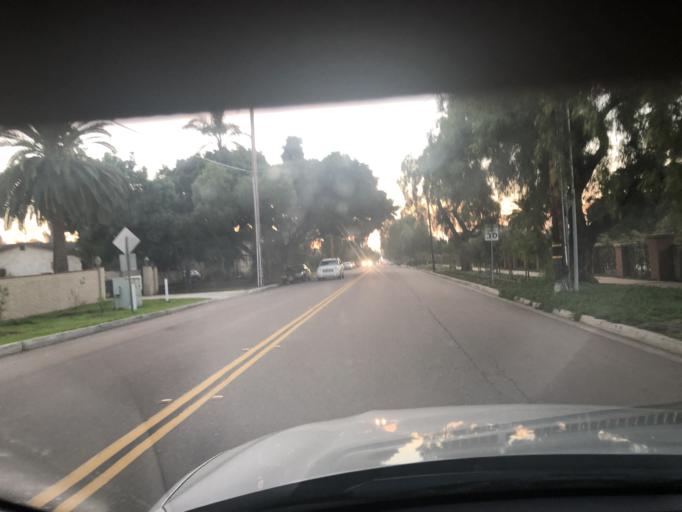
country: US
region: California
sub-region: San Diego County
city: Chula Vista
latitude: 32.6447
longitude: -117.0679
